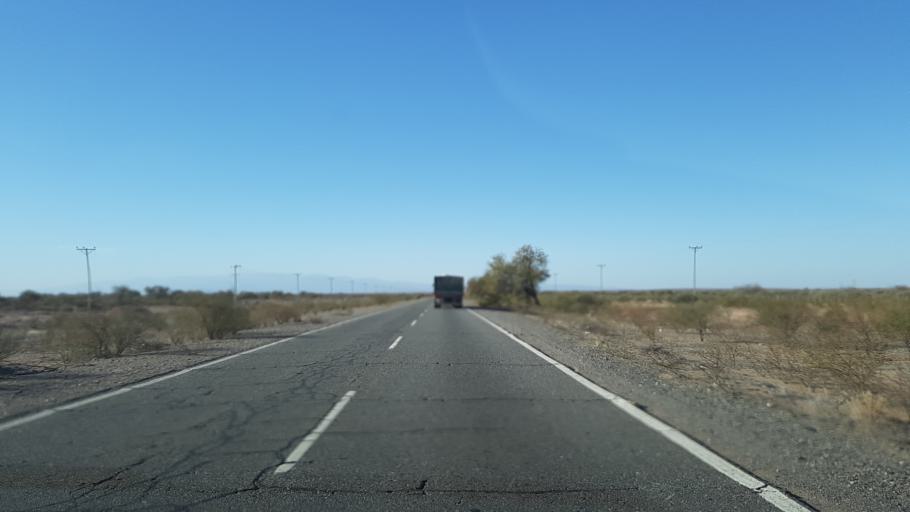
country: AR
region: San Juan
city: Caucete
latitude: -31.6555
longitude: -67.7704
